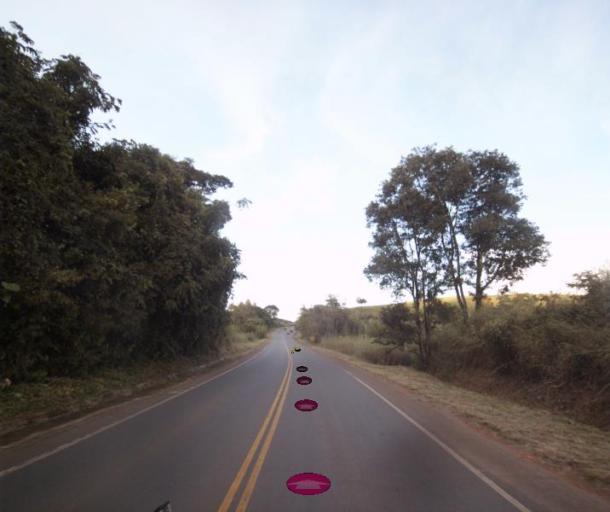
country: BR
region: Goias
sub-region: Abadiania
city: Abadiania
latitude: -16.1067
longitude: -48.8728
